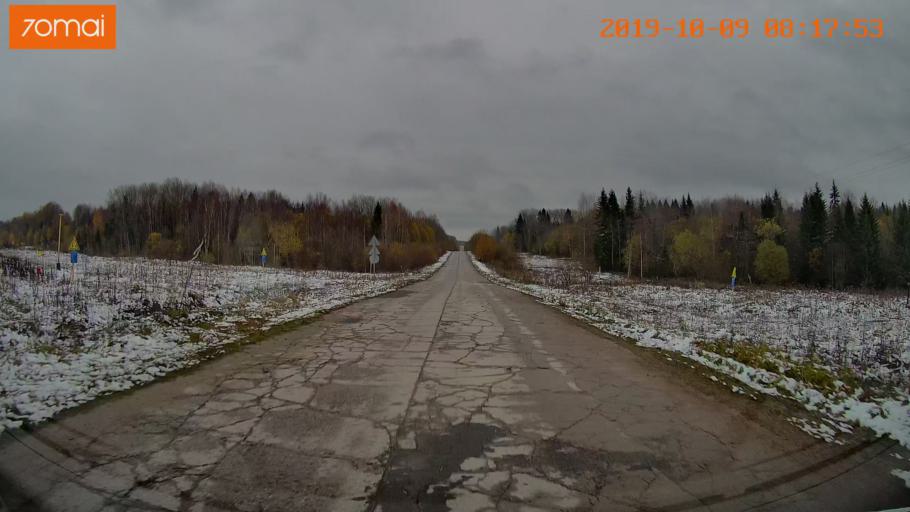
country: RU
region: Vologda
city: Gryazovets
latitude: 58.7394
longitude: 40.2133
